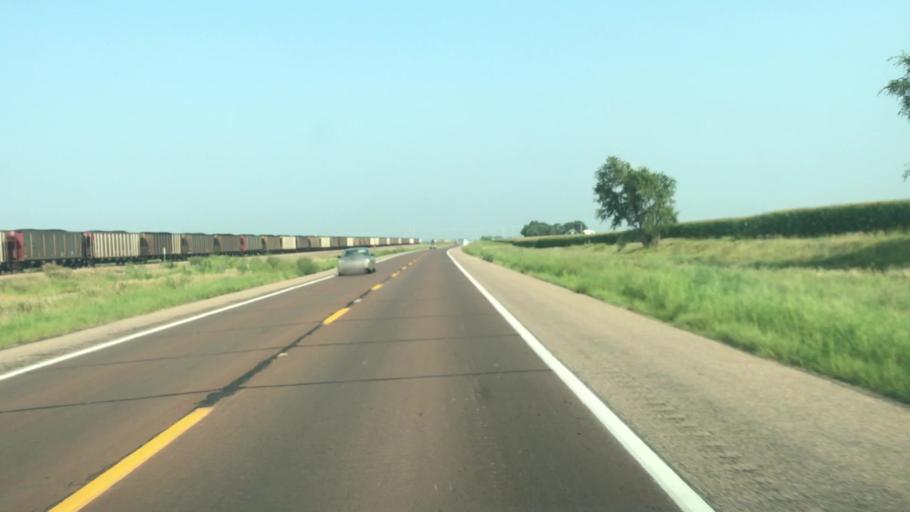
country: US
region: Nebraska
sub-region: Hall County
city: Wood River
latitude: 40.9999
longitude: -98.5977
